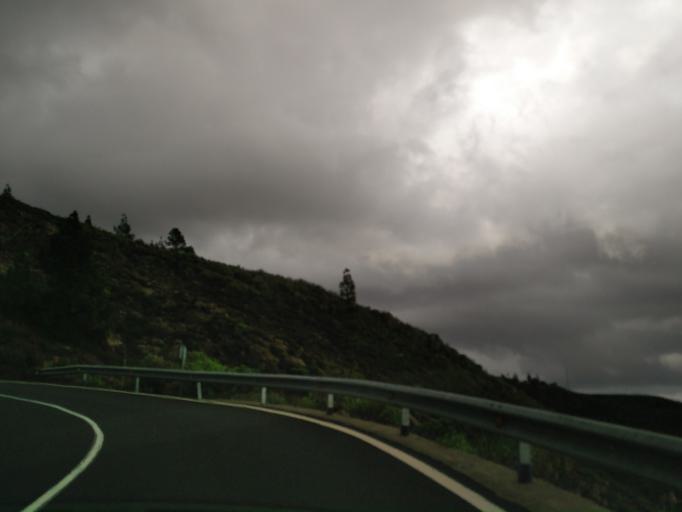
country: ES
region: Canary Islands
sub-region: Provincia de Santa Cruz de Tenerife
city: Arona
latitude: 28.1160
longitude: -16.6778
